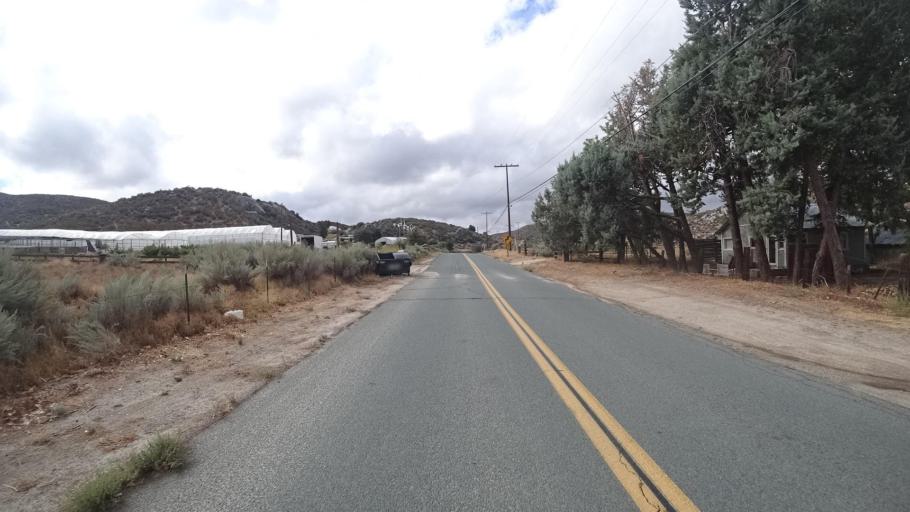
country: US
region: California
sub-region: San Diego County
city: Campo
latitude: 32.7230
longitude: -116.4271
